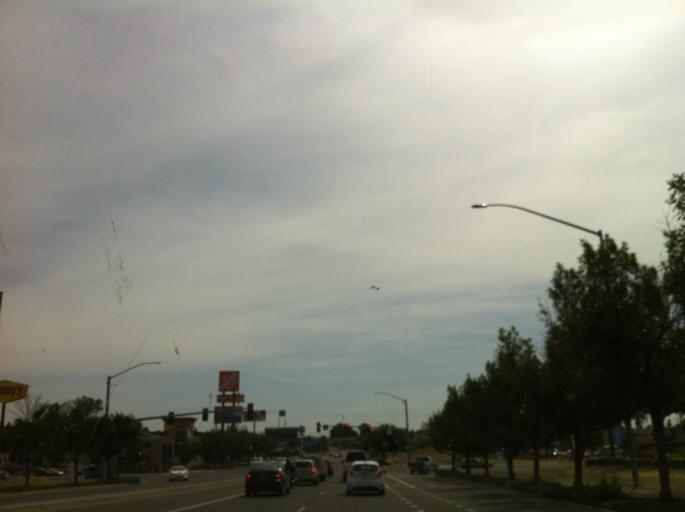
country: US
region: Oregon
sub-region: Malheur County
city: Ontario
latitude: 44.0247
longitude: -116.9477
